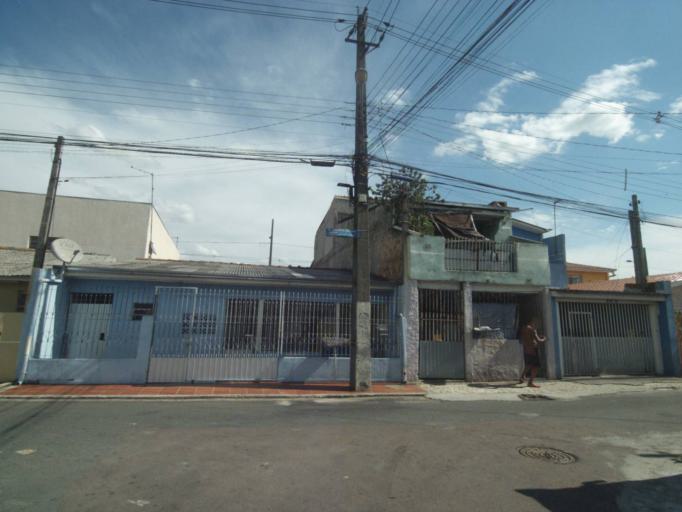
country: BR
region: Parana
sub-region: Curitiba
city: Curitiba
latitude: -25.5160
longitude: -49.3317
